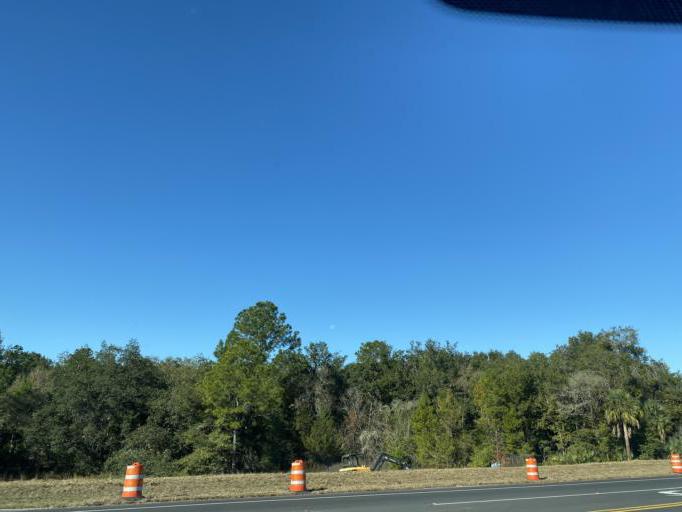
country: US
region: Florida
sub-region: Lake County
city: Mount Plymouth
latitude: 28.8297
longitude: -81.5212
